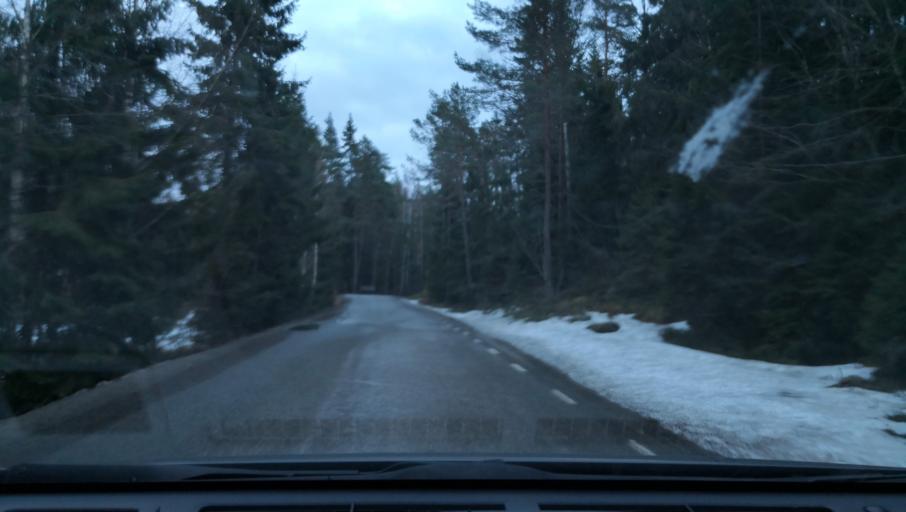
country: SE
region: Vaestmanland
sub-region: Kopings Kommun
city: Kolsva
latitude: 59.5681
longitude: 15.7776
